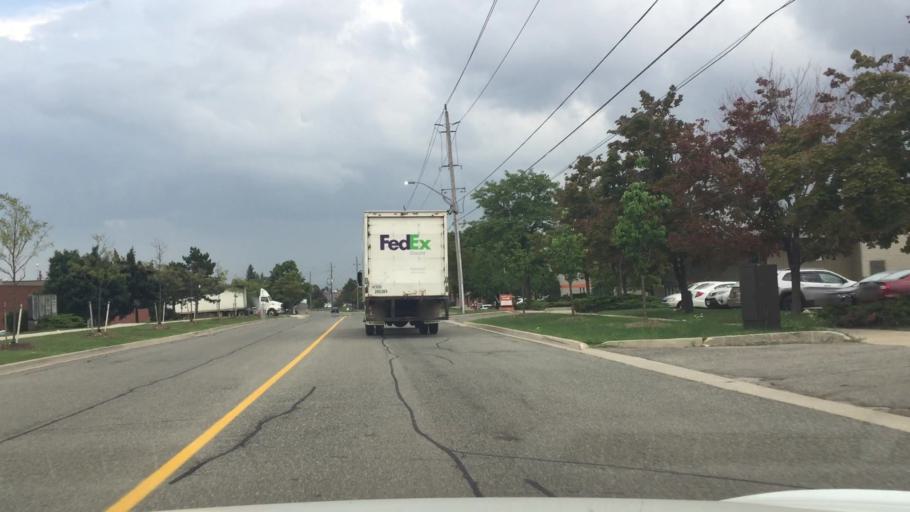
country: CA
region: Ontario
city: Mississauga
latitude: 43.6306
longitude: -79.6439
